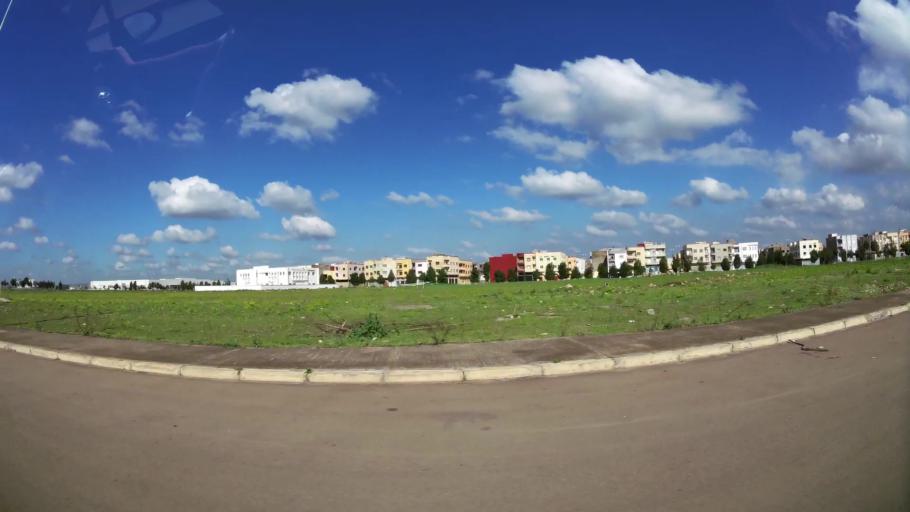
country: MA
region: Grand Casablanca
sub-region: Mediouna
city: Mediouna
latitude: 33.3889
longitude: -7.5489
